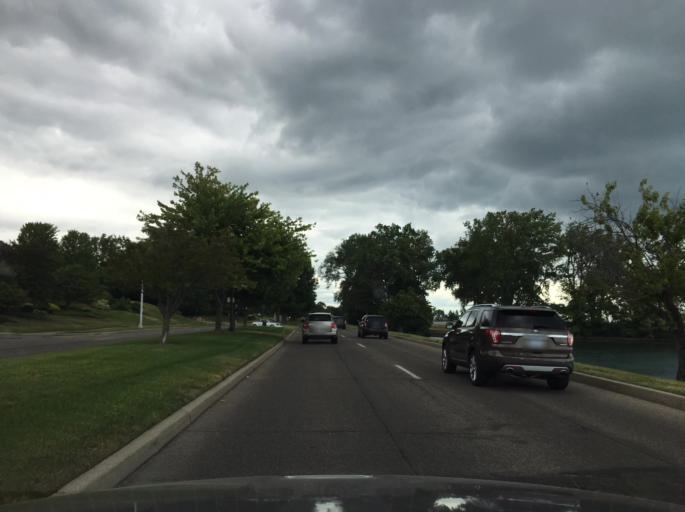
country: US
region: Michigan
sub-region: Wayne County
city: Grosse Pointe Farms
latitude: 42.3966
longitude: -82.8895
